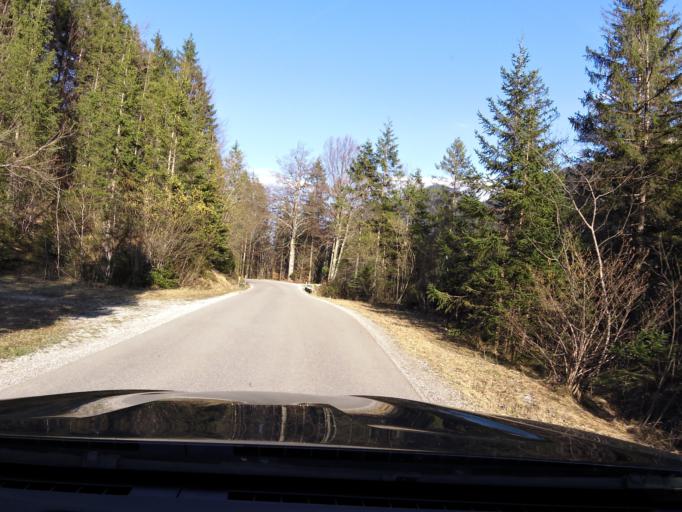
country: DE
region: Bavaria
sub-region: Upper Bavaria
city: Wallgau
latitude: 47.5393
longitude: 11.3383
